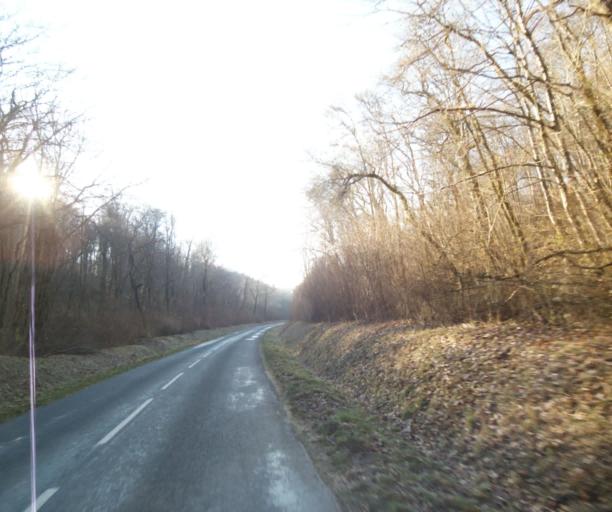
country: FR
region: Champagne-Ardenne
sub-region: Departement de la Haute-Marne
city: Chevillon
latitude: 48.5361
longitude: 5.1924
